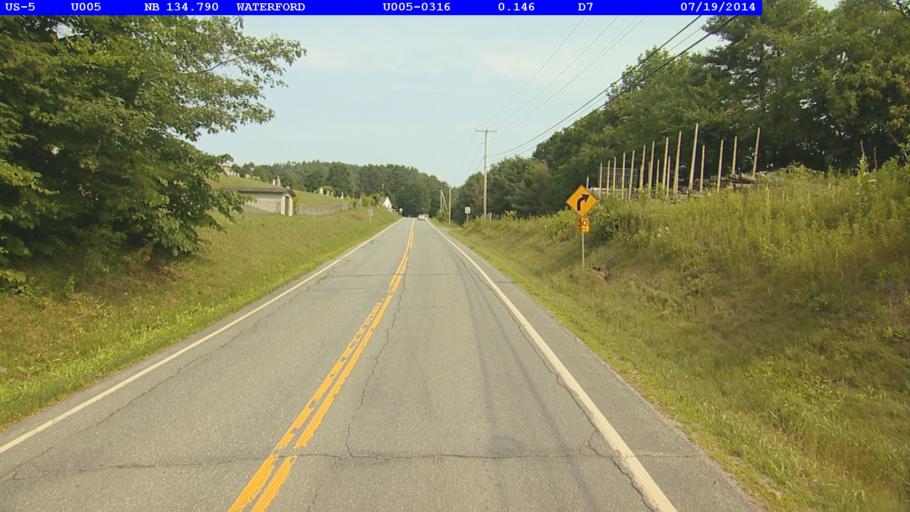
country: US
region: Vermont
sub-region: Caledonia County
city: Saint Johnsbury
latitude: 44.3814
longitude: -72.0262
